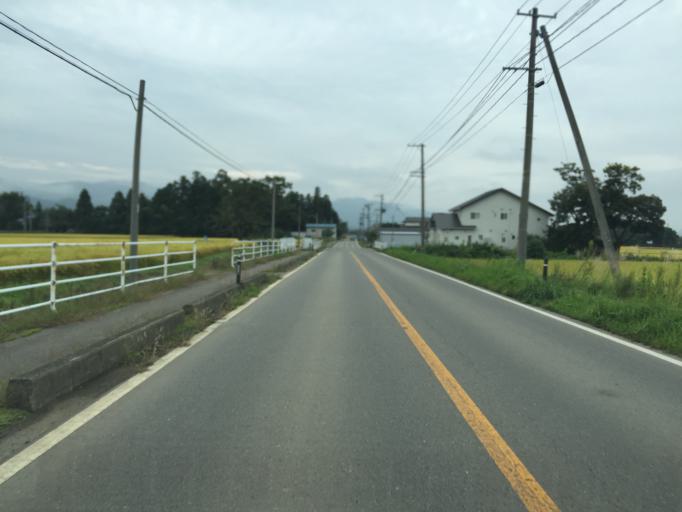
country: JP
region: Fukushima
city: Kitakata
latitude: 37.5358
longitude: 139.9304
